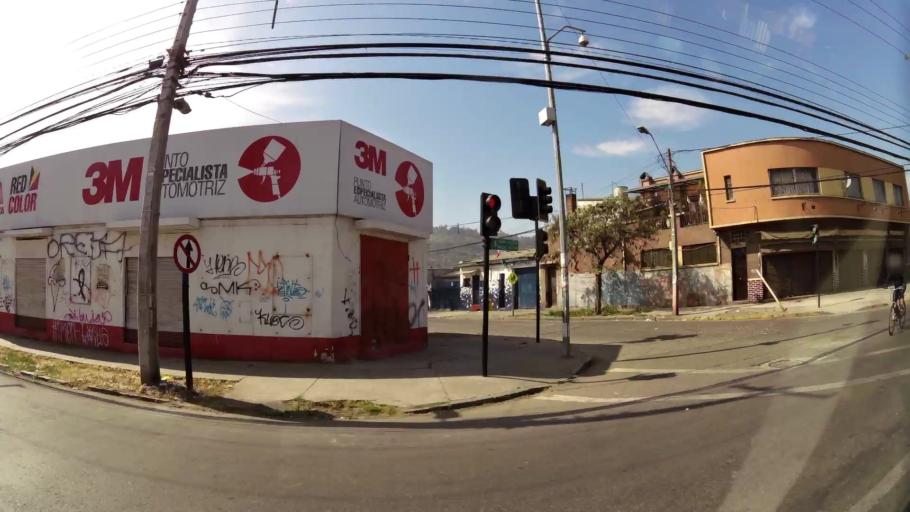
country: CL
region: Santiago Metropolitan
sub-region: Provincia de Santiago
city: Santiago
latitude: -33.4039
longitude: -70.6319
